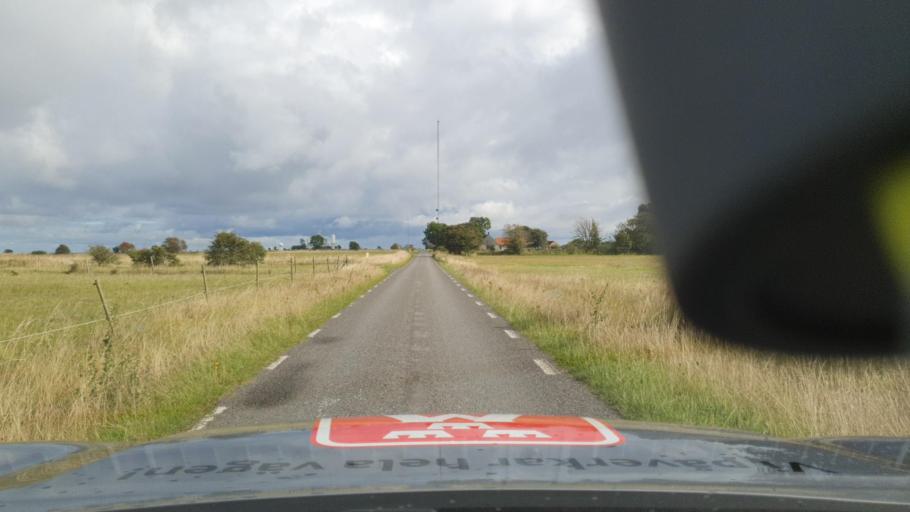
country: SE
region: Gotland
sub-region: Gotland
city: Hemse
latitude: 57.0014
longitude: 18.3735
